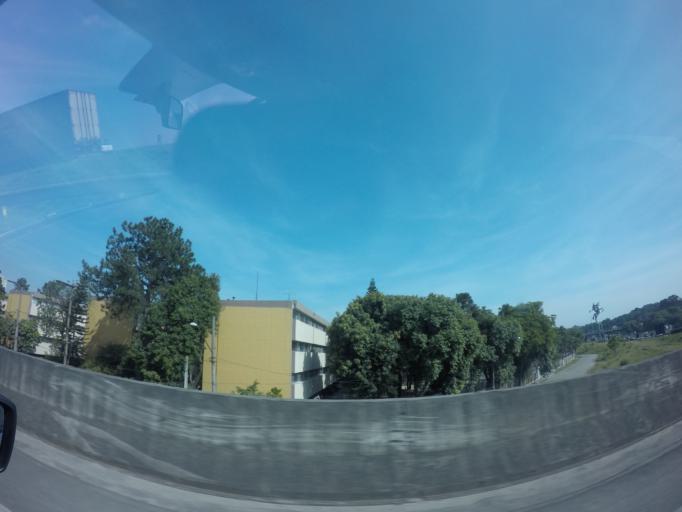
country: BR
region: Sao Paulo
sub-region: Guarulhos
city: Guarulhos
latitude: -23.4620
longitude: -46.4922
